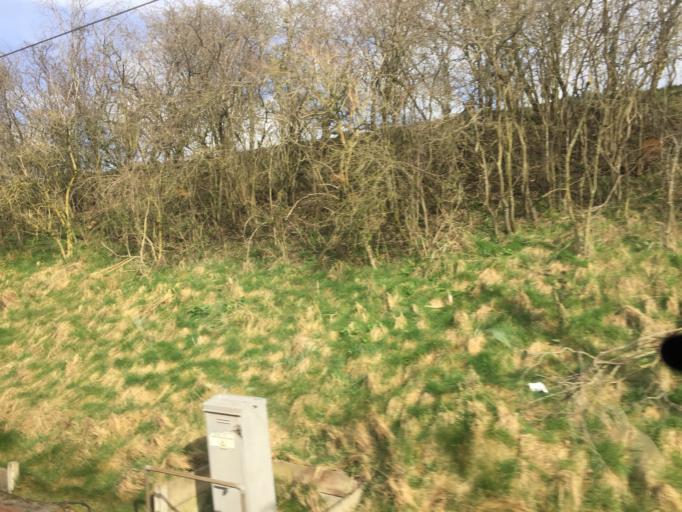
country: GB
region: England
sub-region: Cumbria
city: Penrith
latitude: 54.6377
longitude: -2.7467
